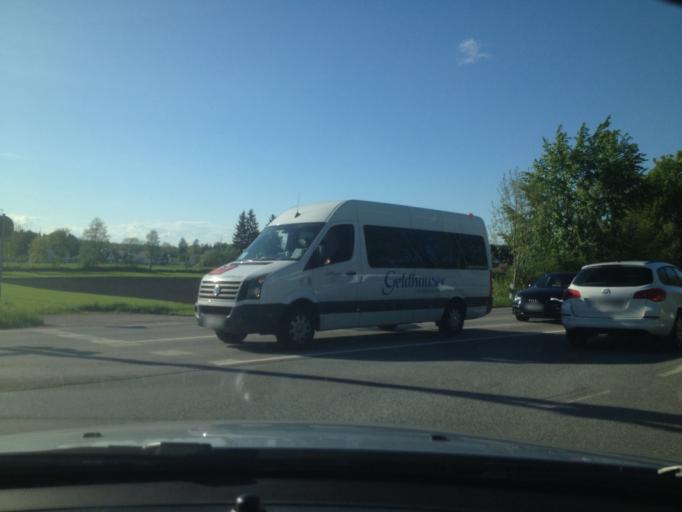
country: DE
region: Bavaria
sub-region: Swabia
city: Bobingen
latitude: 48.3091
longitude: 10.8548
